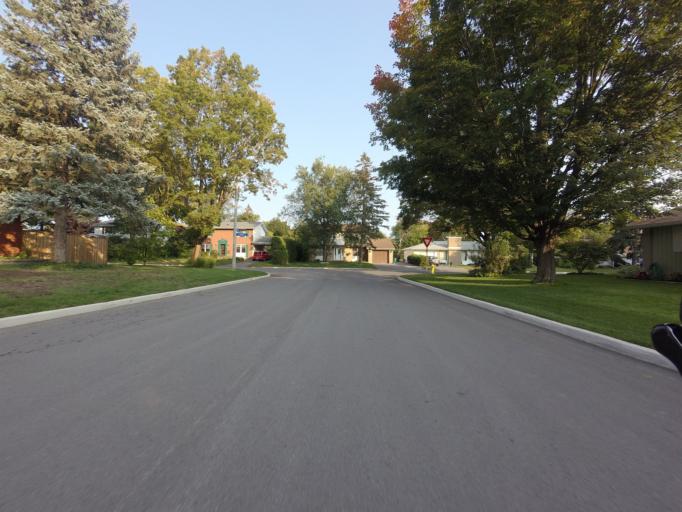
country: CA
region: Ontario
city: Bells Corners
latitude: 45.2982
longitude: -75.8805
